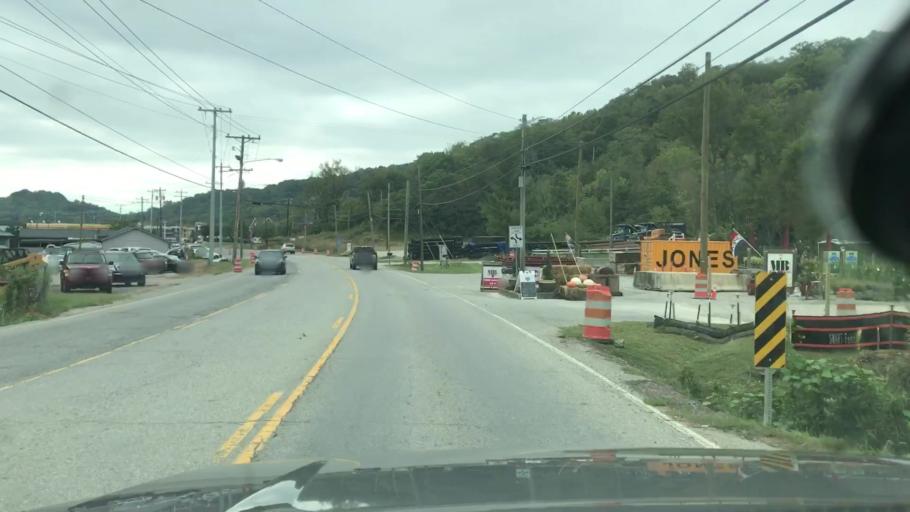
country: US
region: Tennessee
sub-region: Williamson County
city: Franklin
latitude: 35.9758
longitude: -86.8300
